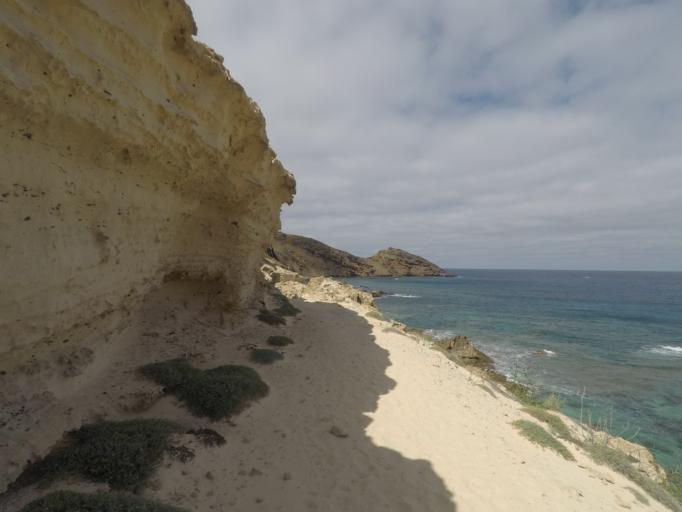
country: PT
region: Madeira
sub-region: Porto Santo
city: Vila de Porto Santo
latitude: 33.0725
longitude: -16.2964
